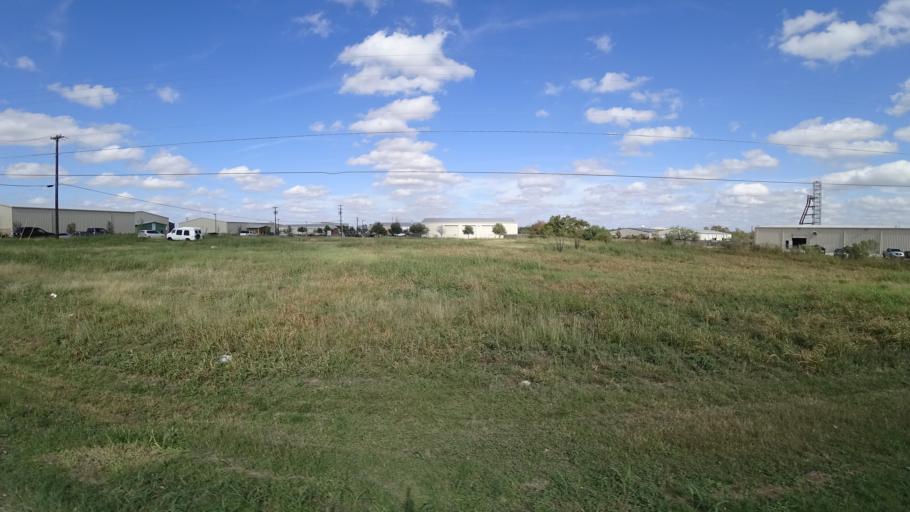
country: US
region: Texas
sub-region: Travis County
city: Windemere
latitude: 30.4670
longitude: -97.6632
